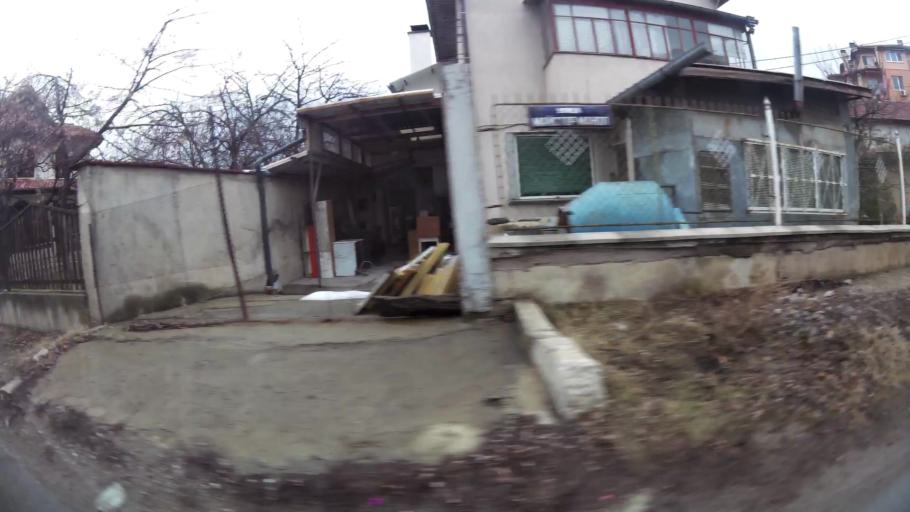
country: BG
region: Sofia-Capital
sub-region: Stolichna Obshtina
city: Sofia
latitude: 42.7269
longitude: 23.2642
